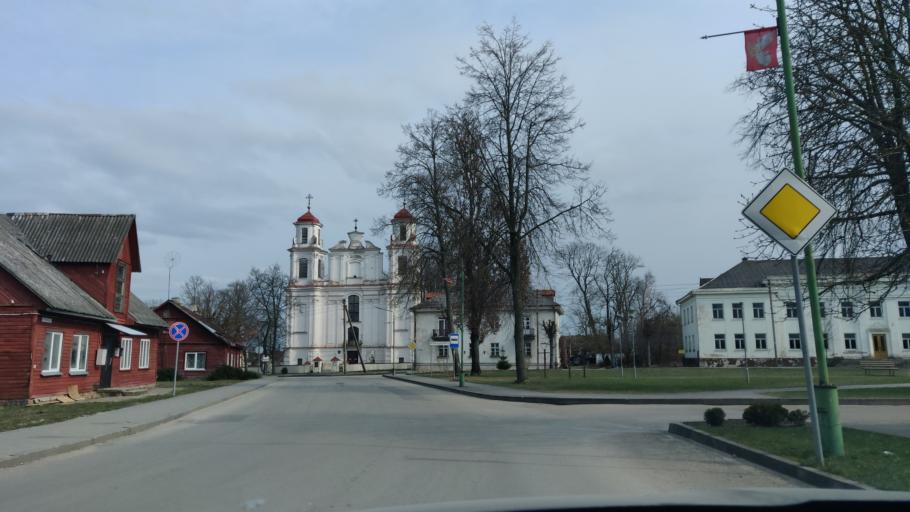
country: LT
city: Jieznas
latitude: 54.5994
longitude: 24.1718
